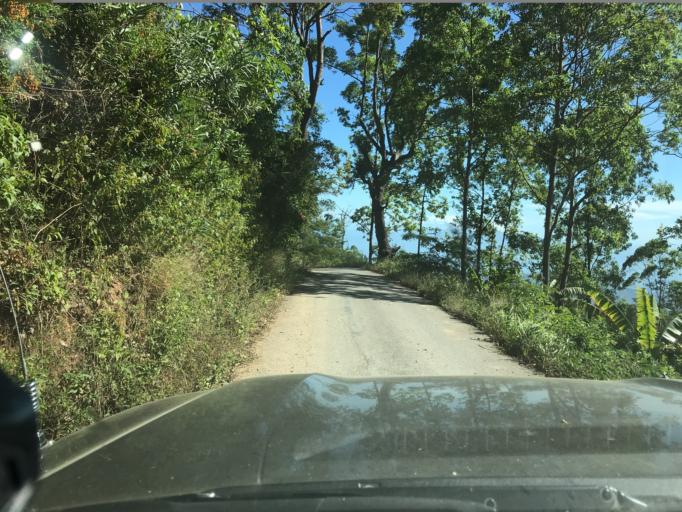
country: TL
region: Dili
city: Dili
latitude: -8.6207
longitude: 125.6358
